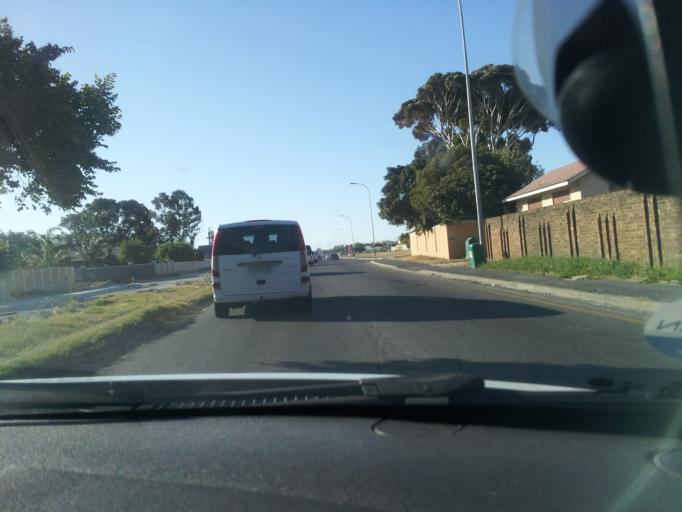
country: ZA
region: Western Cape
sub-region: Cape Winelands District Municipality
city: Stellenbosch
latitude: -34.1032
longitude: 18.8331
